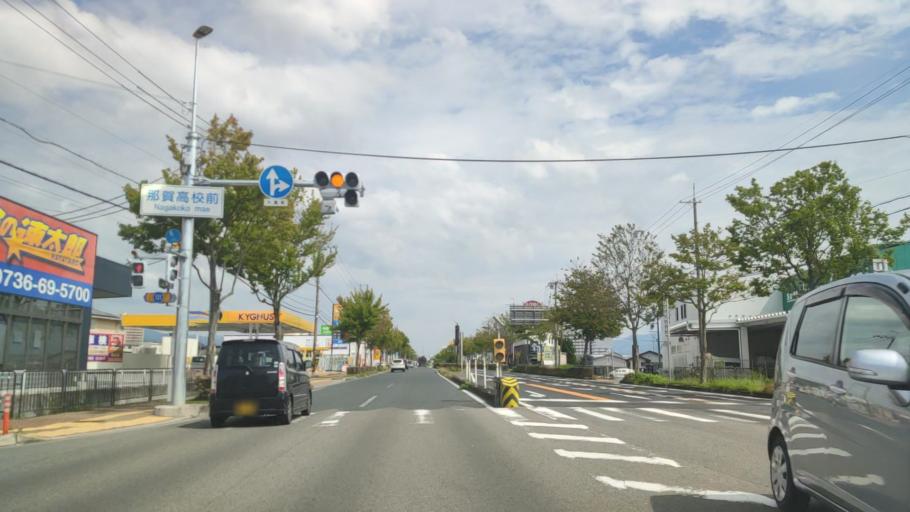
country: JP
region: Wakayama
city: Iwade
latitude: 34.2624
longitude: 135.3236
